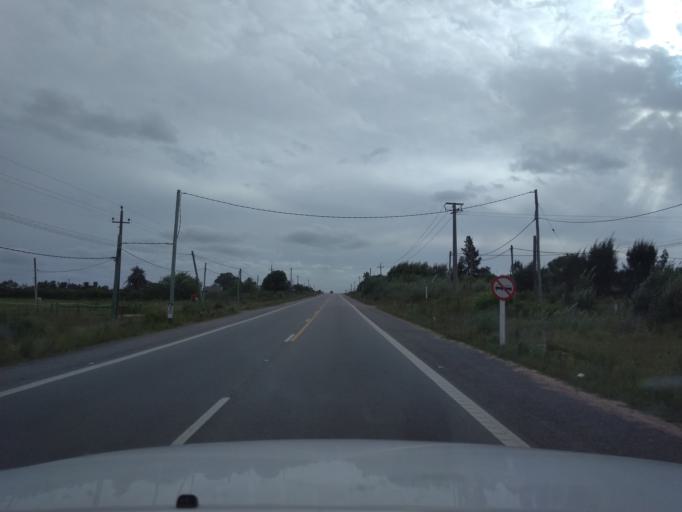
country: UY
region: Canelones
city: Joaquin Suarez
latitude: -34.6979
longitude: -56.0368
